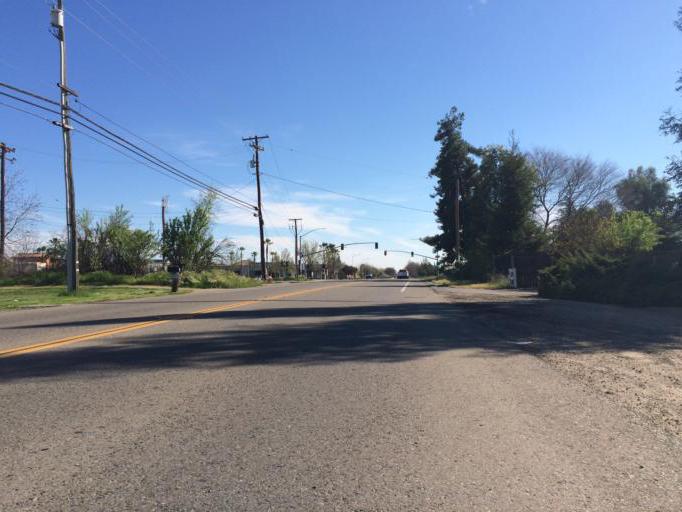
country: US
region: California
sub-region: Fresno County
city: Clovis
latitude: 36.8532
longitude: -119.6841
